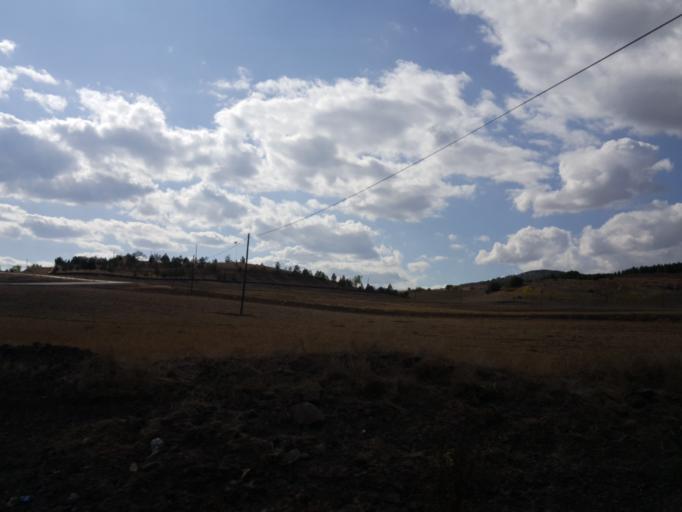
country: TR
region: Tokat
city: Sulusaray
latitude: 39.9763
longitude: 36.0137
